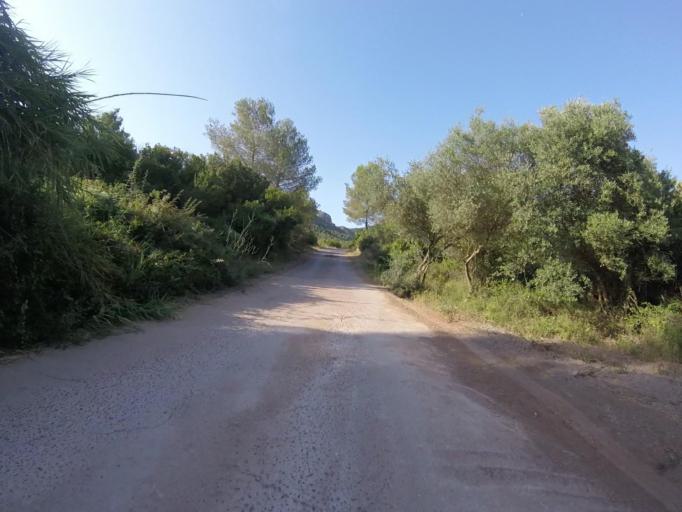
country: ES
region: Valencia
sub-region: Provincia de Castello
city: Benicassim
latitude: 40.0962
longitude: 0.0624
